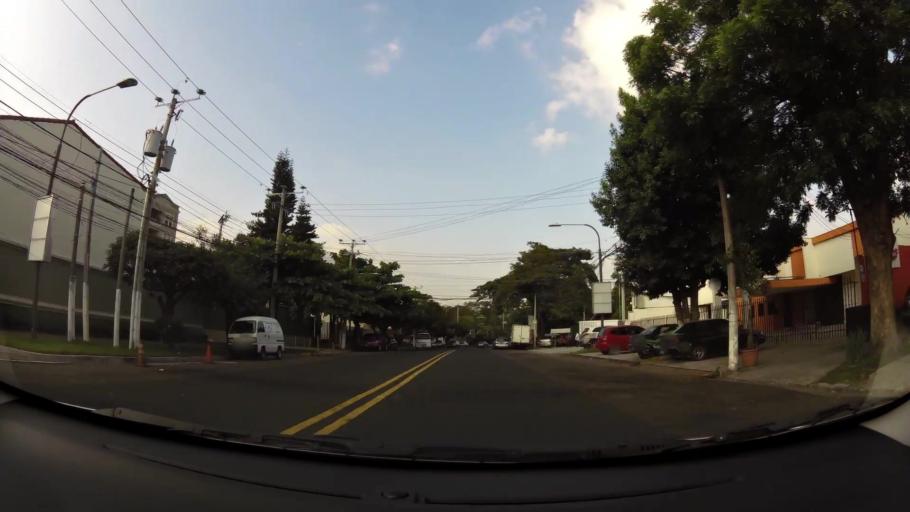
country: SV
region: La Libertad
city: Antiguo Cuscatlan
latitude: 13.6932
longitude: -89.2439
